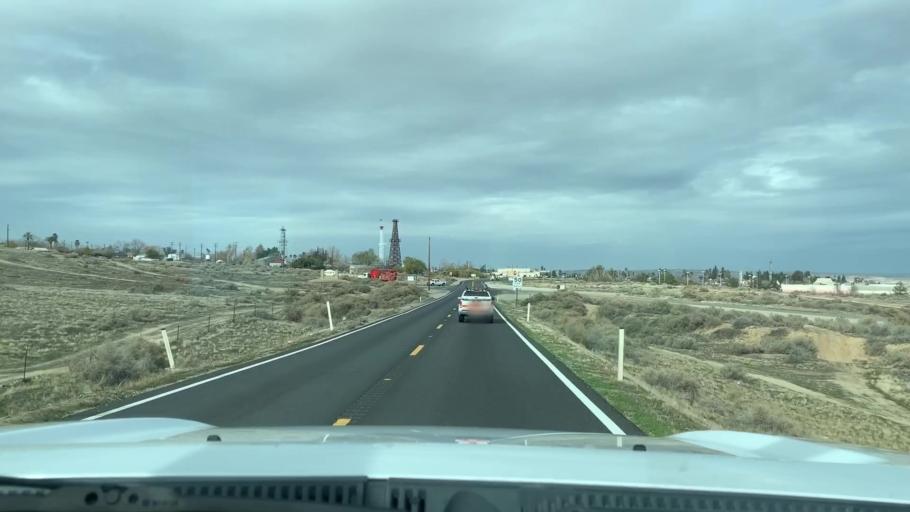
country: US
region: California
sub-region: Kern County
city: South Taft
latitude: 35.1303
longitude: -119.4443
